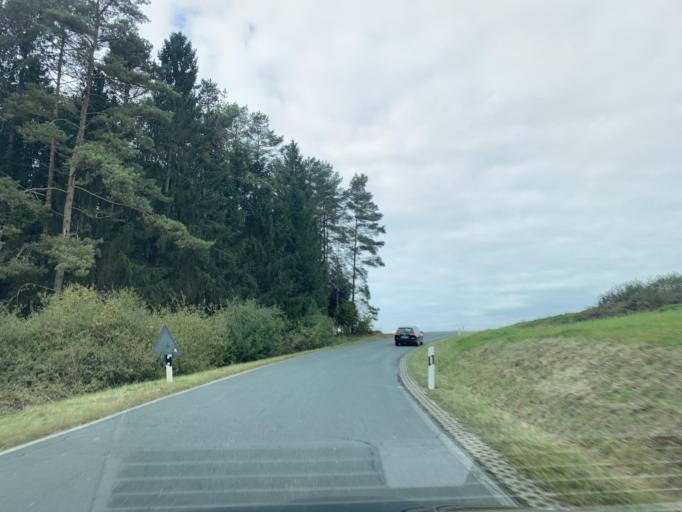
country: DE
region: Bavaria
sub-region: Upper Franconia
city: Pottenstein
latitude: 49.7390
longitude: 11.4071
